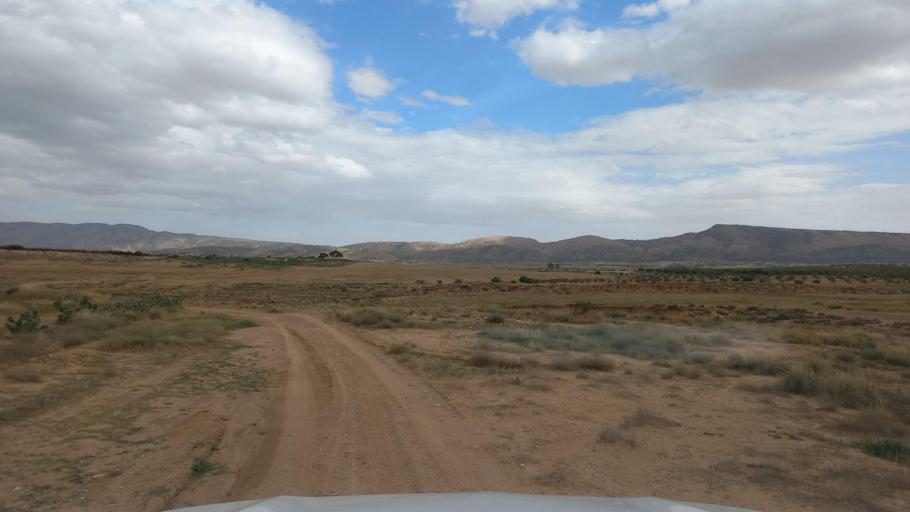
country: TN
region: Al Qasrayn
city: Sbiba
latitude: 35.3781
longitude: 9.1218
